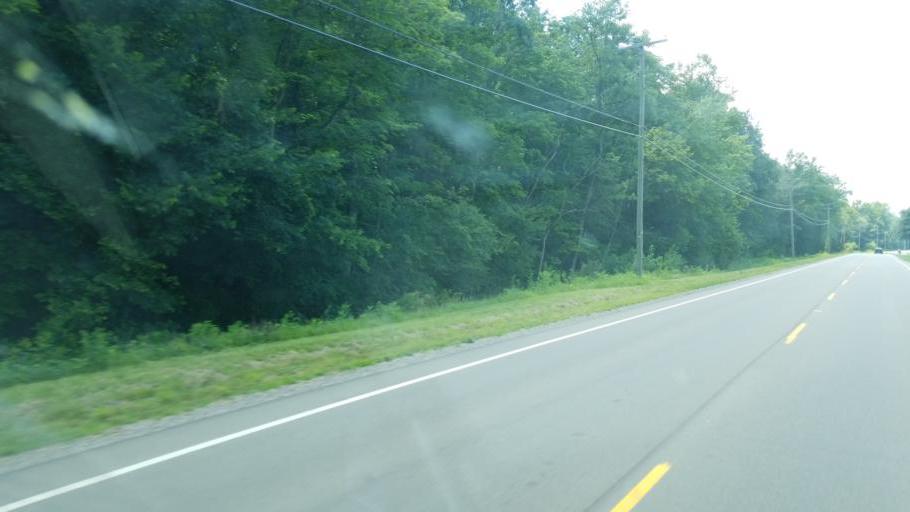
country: US
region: Ohio
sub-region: Coshocton County
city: Coshocton
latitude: 40.3049
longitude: -81.9211
